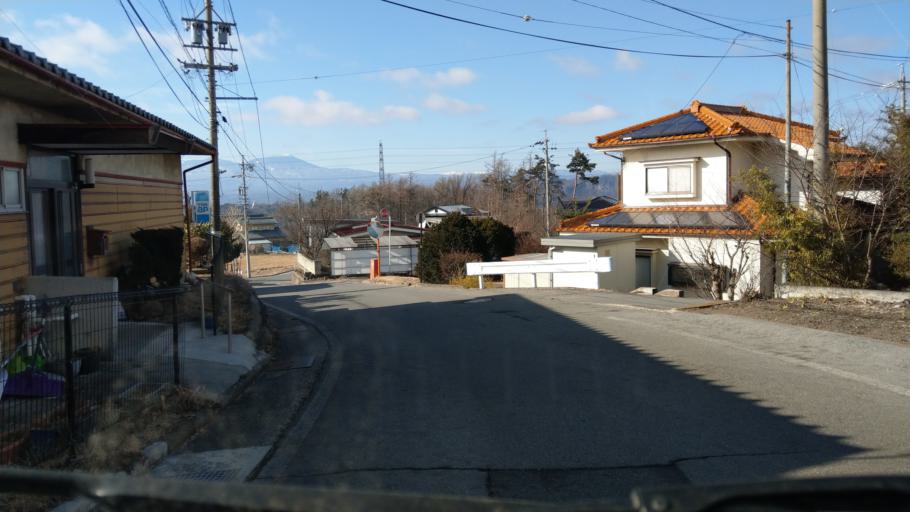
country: JP
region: Nagano
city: Komoro
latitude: 36.3237
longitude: 138.4440
